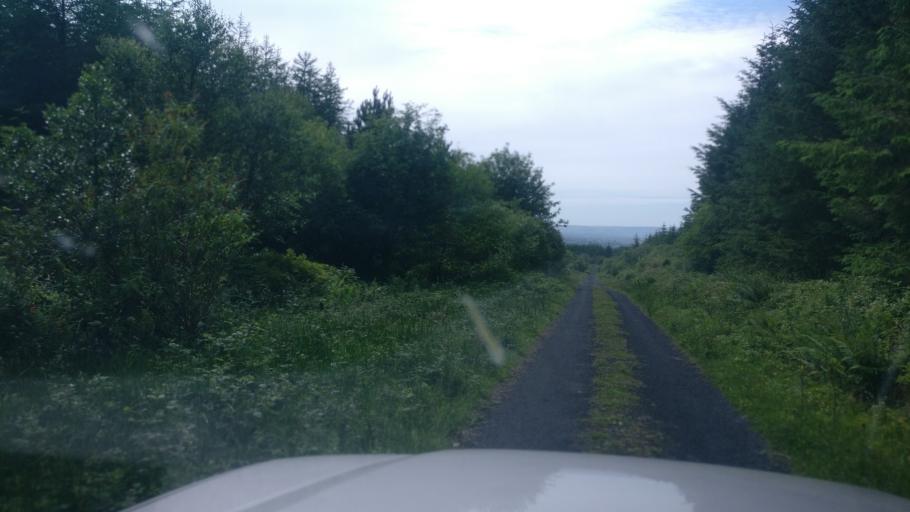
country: IE
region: Connaught
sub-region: County Galway
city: Gort
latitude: 53.0637
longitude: -8.6894
